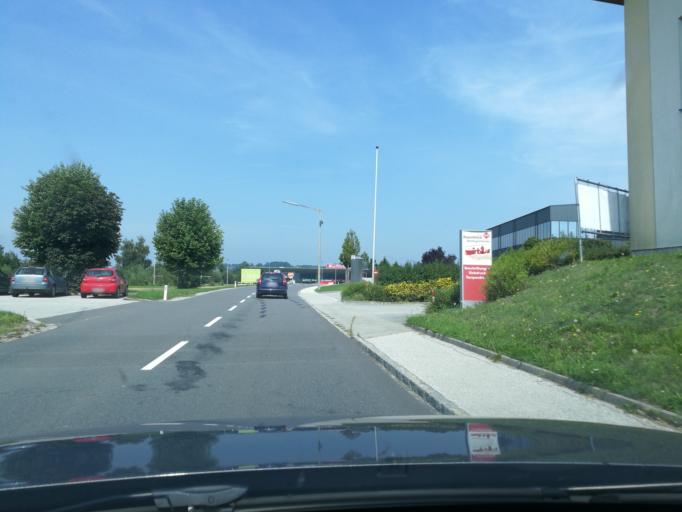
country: AT
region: Upper Austria
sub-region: Politischer Bezirk Grieskirchen
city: Grieskirchen
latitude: 48.3311
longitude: 13.7717
